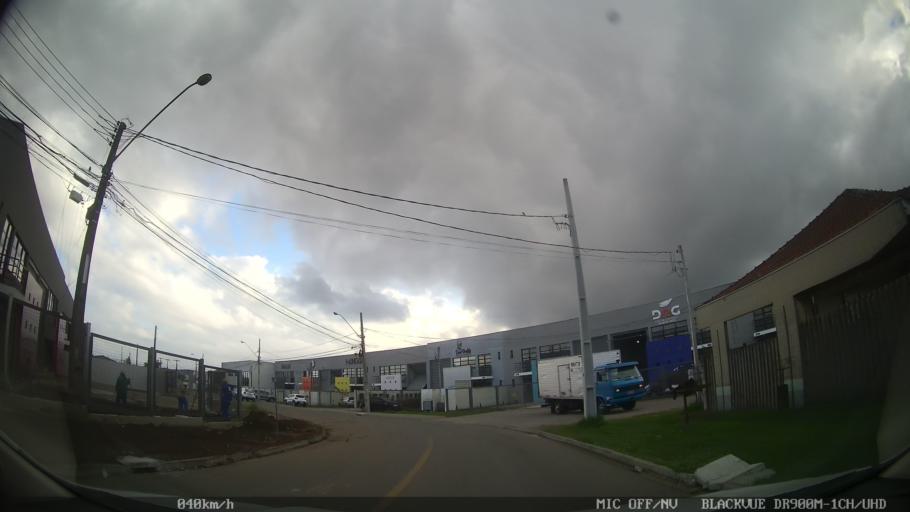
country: BR
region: Parana
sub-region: Pinhais
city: Pinhais
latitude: -25.4356
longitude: -49.1950
